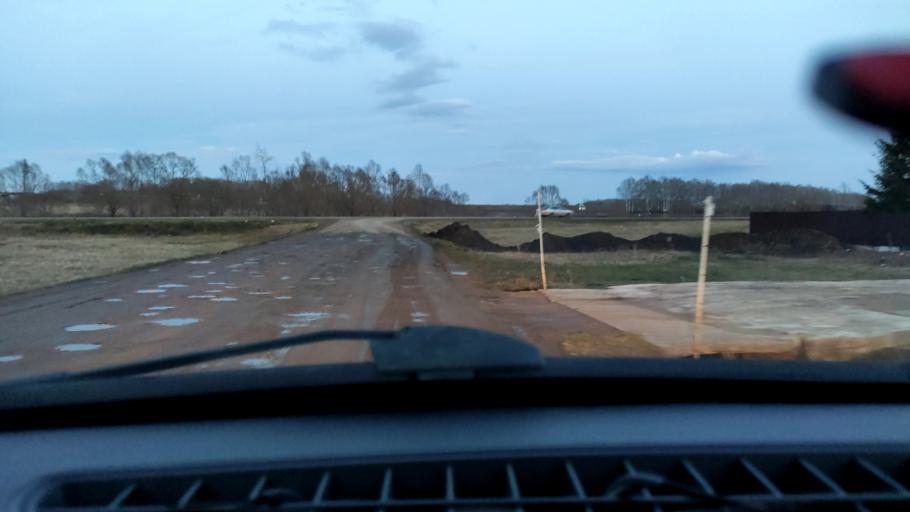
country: RU
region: Bashkortostan
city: Ulukulevo
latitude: 54.4196
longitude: 56.3420
